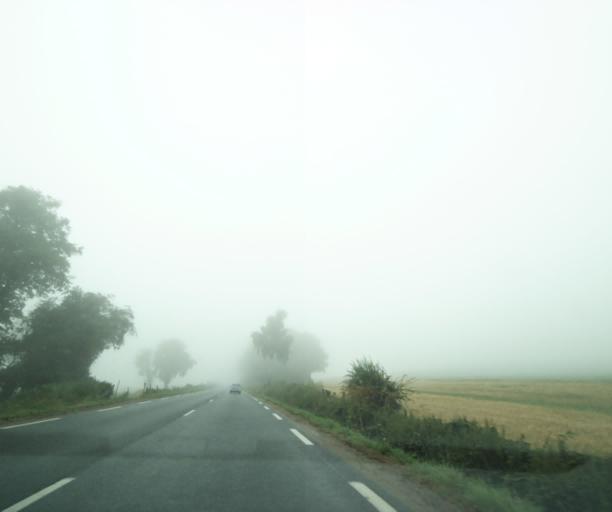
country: FR
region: Midi-Pyrenees
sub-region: Departement de l'Aveyron
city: Baraqueville
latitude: 44.2581
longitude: 2.4160
